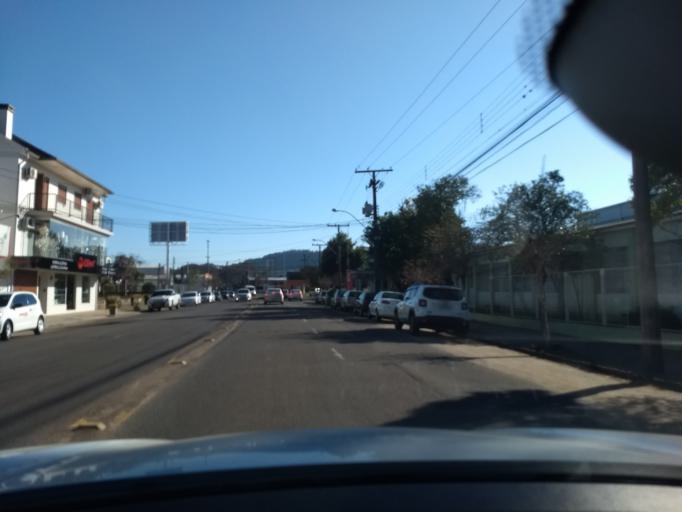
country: BR
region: Rio Grande do Sul
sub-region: Santa Cruz Do Sul
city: Santa Cruz do Sul
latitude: -29.7093
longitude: -52.4356
